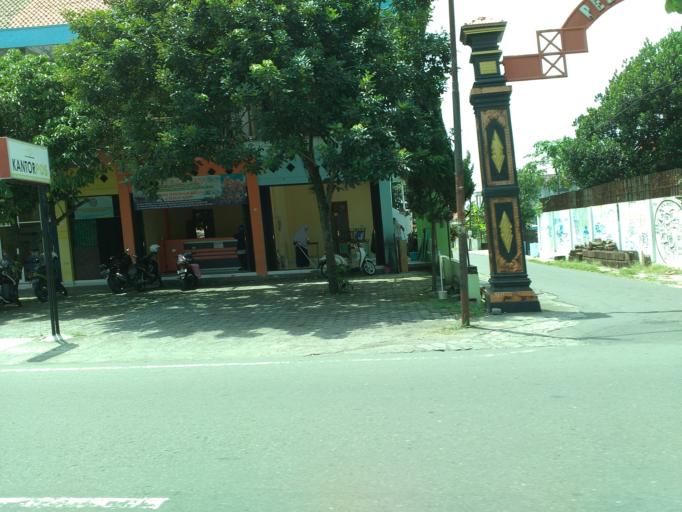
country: ID
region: Central Java
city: Klaten
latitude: -7.6893
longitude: 110.6100
